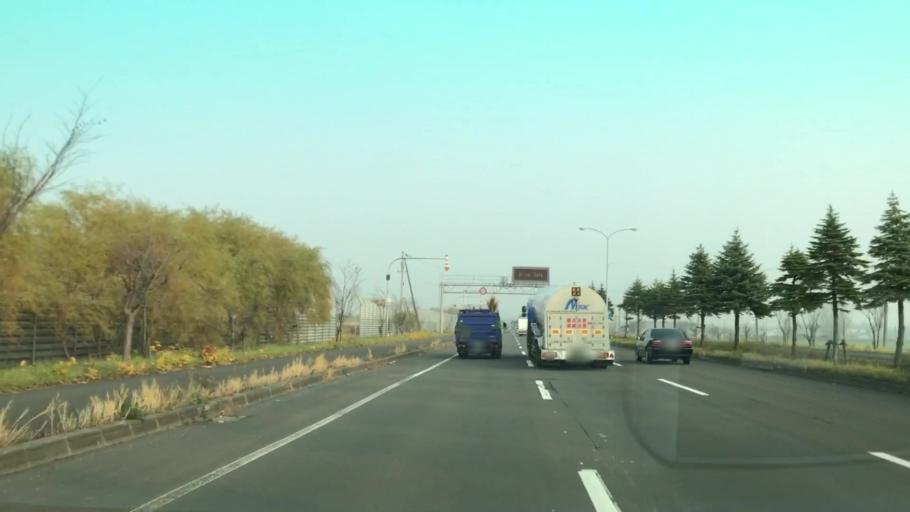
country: JP
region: Hokkaido
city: Ishikari
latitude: 43.1711
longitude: 141.3485
